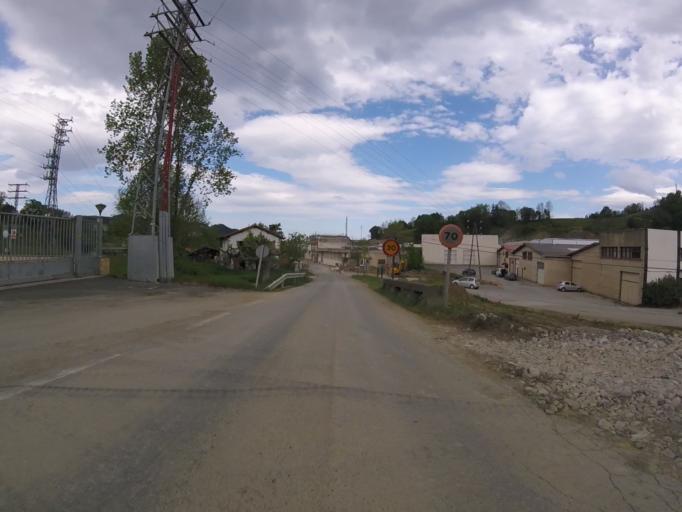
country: ES
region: Basque Country
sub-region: Provincia de Guipuzcoa
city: Zarautz
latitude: 43.2732
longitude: -2.1690
